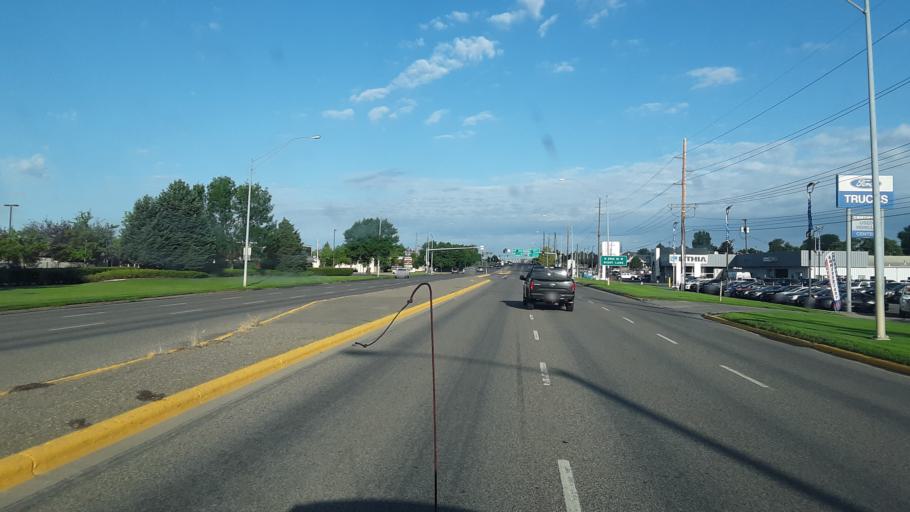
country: US
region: Montana
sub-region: Yellowstone County
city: Billings
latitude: 45.7552
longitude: -108.5703
